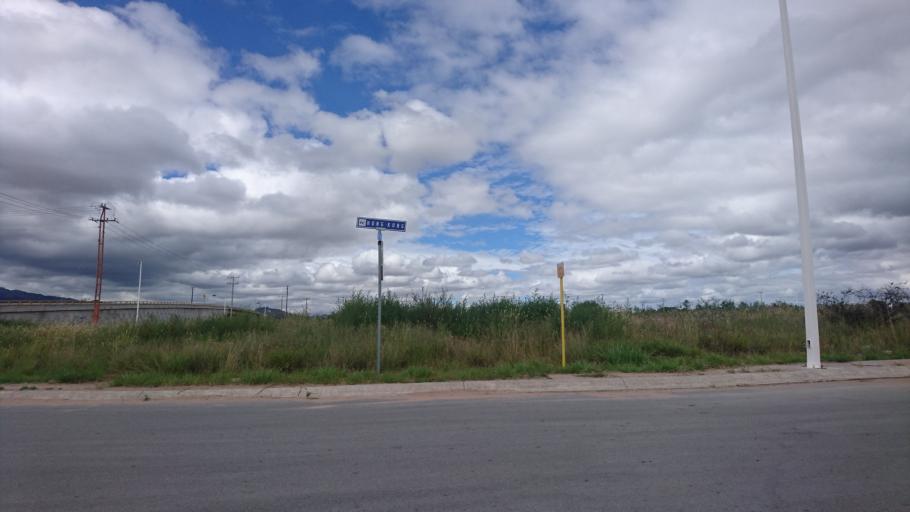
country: MX
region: San Luis Potosi
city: La Pila
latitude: 21.9911
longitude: -100.8609
